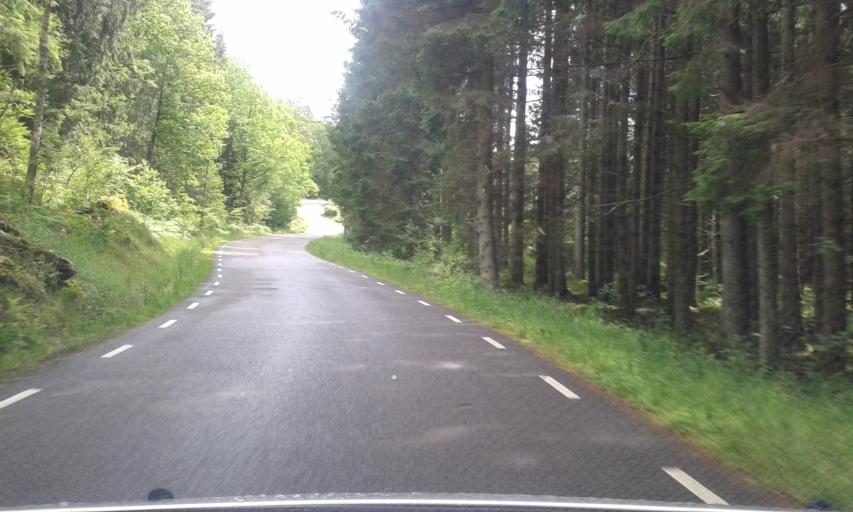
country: SE
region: Vaestra Goetaland
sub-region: Kungalvs Kommun
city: Diserod
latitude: 57.9636
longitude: 12.0013
